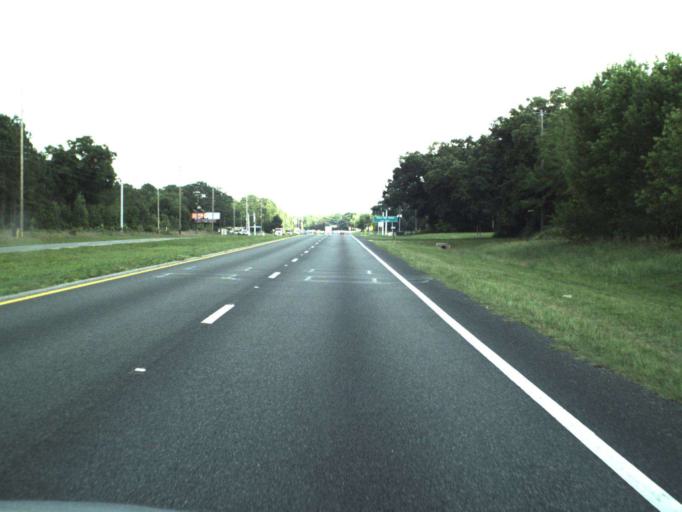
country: US
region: Florida
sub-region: Marion County
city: Silver Springs Shores
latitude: 29.1474
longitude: -82.0699
